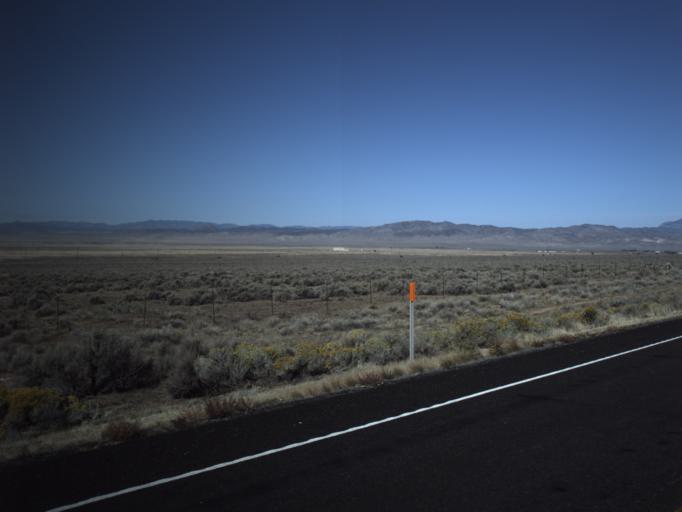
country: US
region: Utah
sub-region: Beaver County
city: Milford
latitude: 38.2395
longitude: -112.9378
